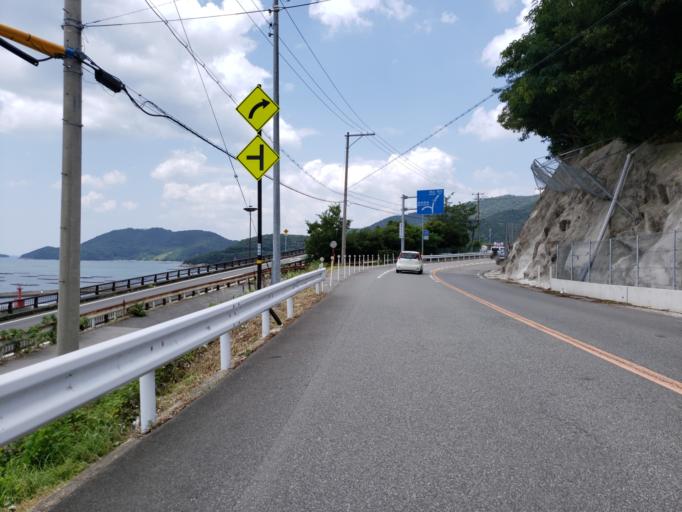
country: JP
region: Hyogo
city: Aioi
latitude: 34.7689
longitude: 134.5030
